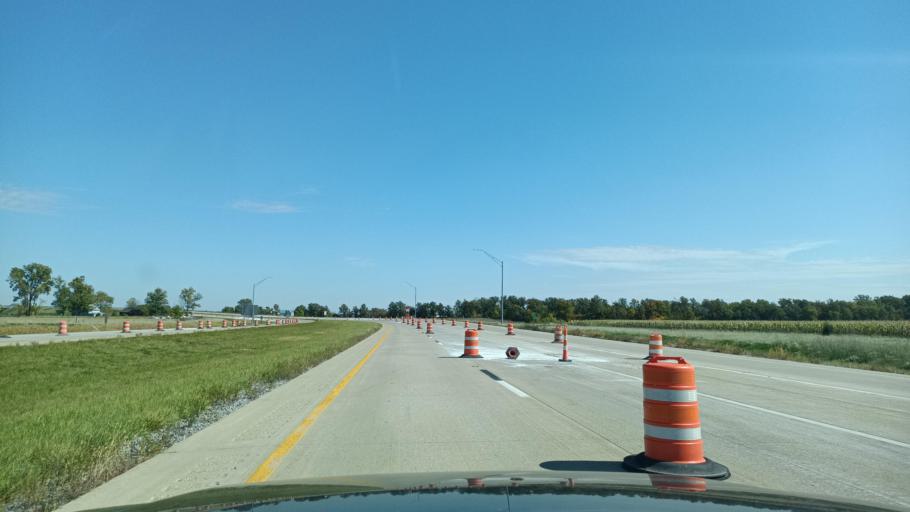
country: US
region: Ohio
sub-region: Paulding County
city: Paulding
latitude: 41.2206
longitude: -84.5780
